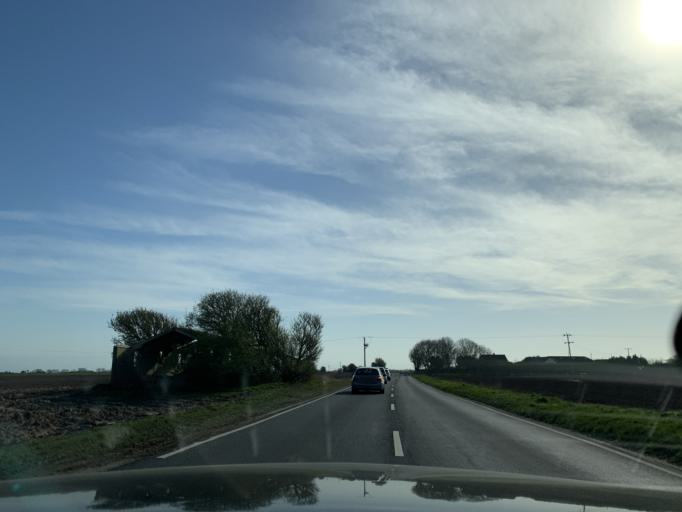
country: GB
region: England
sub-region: Kent
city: New Romney
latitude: 50.9811
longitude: 0.9212
